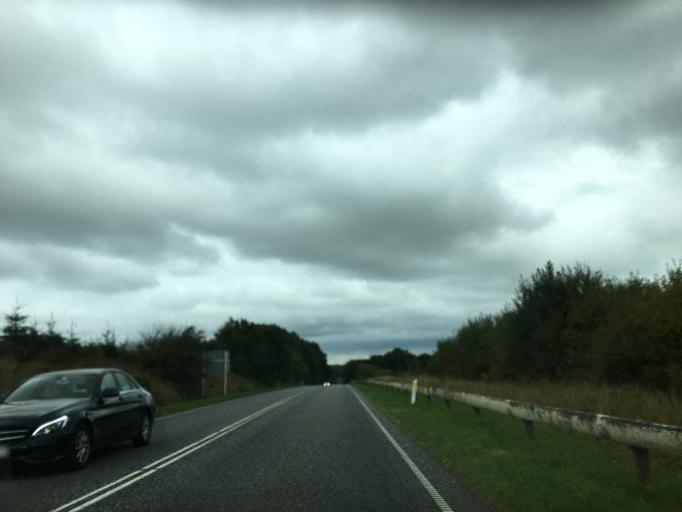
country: DK
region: South Denmark
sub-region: Kolding Kommune
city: Kolding
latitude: 55.5667
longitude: 9.4967
